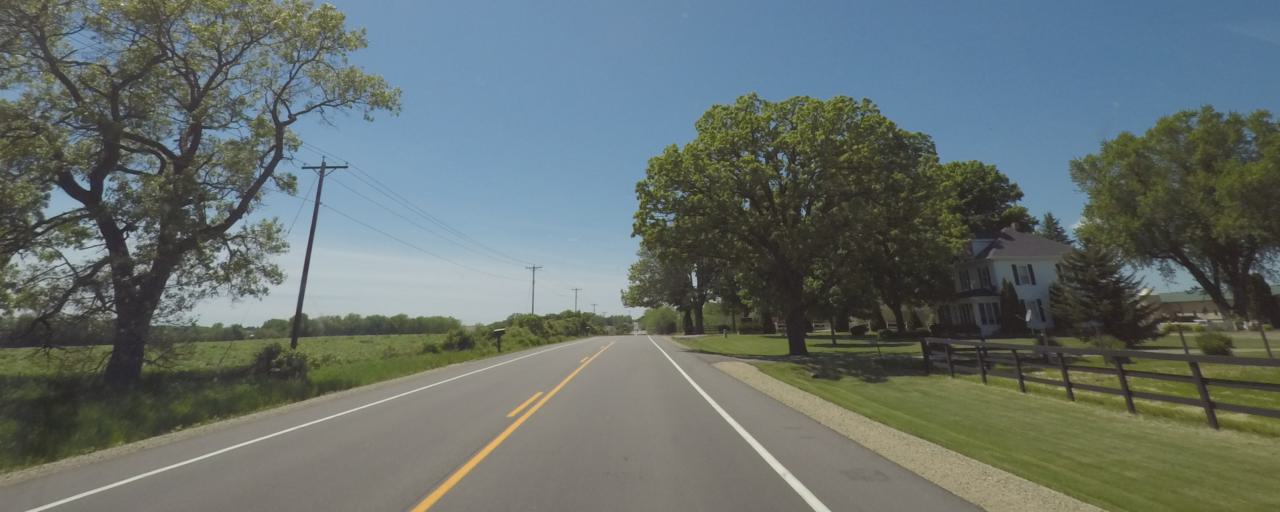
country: US
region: Wisconsin
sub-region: Dane County
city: Fitchburg
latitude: 42.9504
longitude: -89.4270
